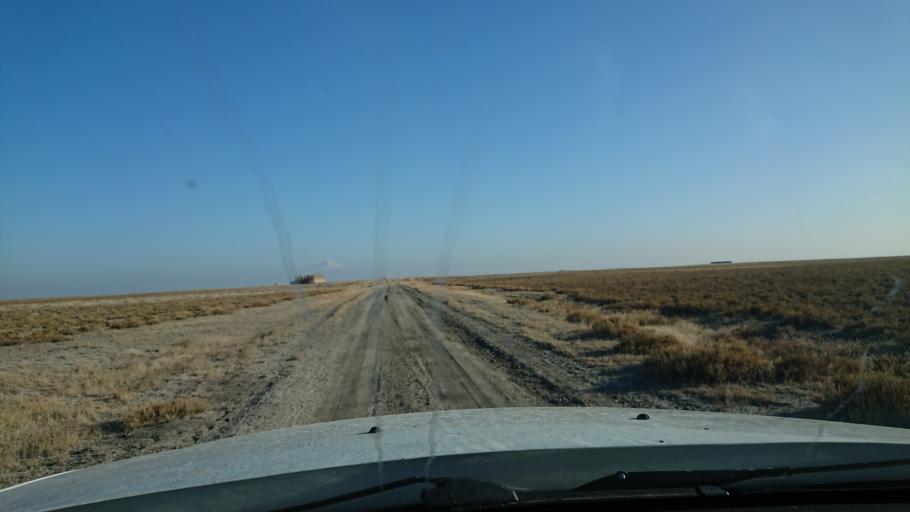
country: TR
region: Aksaray
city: Sultanhani
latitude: 38.3953
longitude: 33.5909
